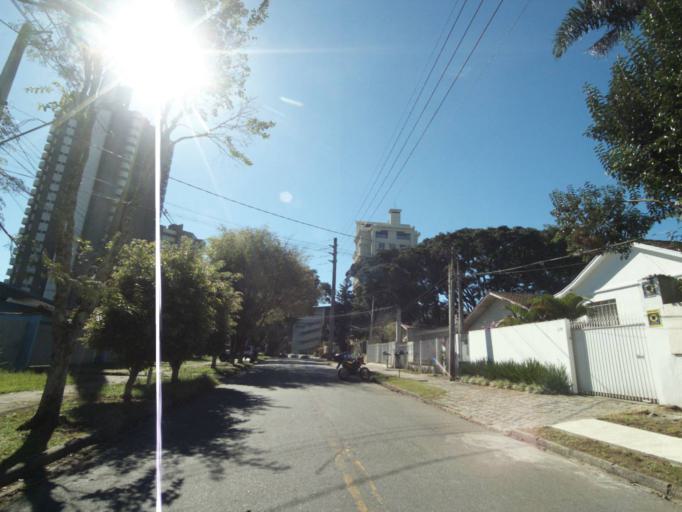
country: BR
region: Parana
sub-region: Curitiba
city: Curitiba
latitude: -25.4118
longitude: -49.2461
